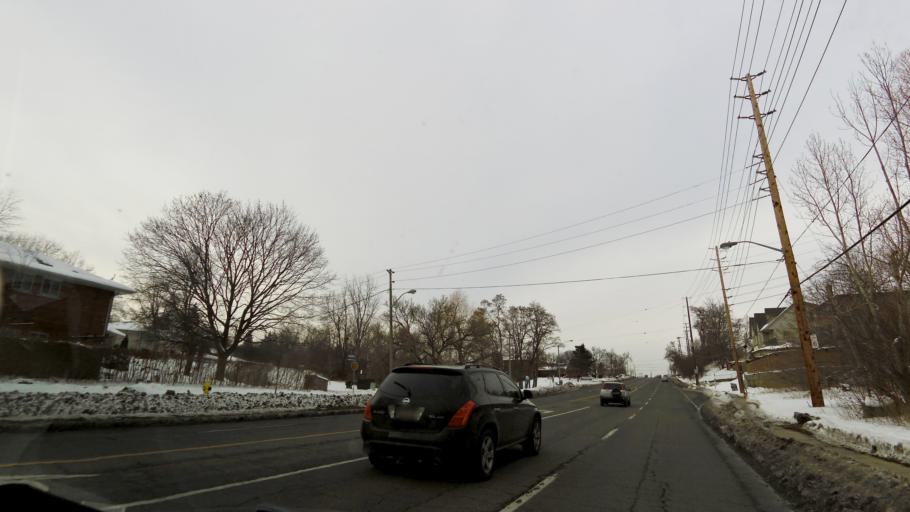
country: CA
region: Ontario
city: Etobicoke
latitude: 43.7337
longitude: -79.5636
